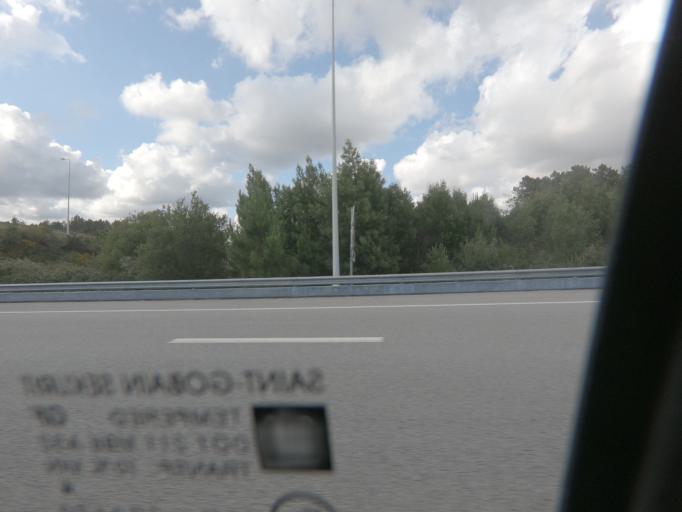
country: PT
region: Porto
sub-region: Valongo
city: Campo
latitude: 41.1832
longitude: -8.4503
